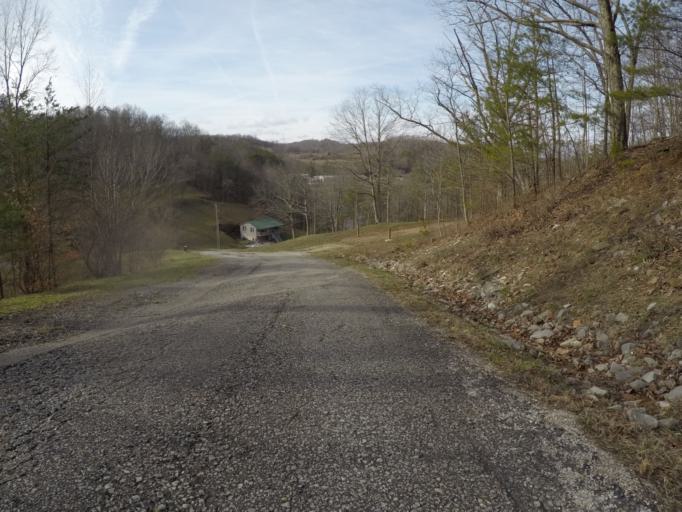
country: US
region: West Virginia
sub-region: Cabell County
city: Huntington
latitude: 38.3859
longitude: -82.3905
